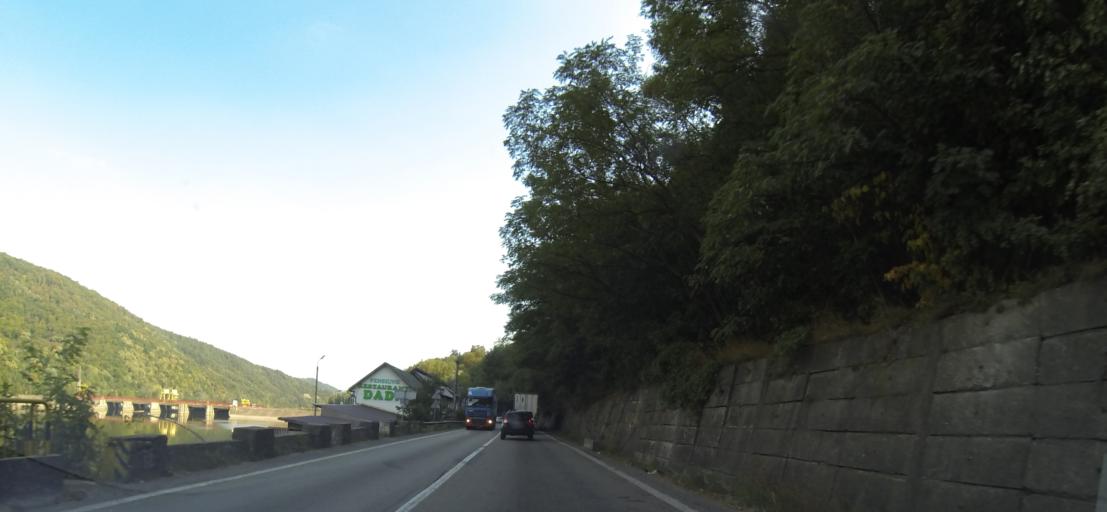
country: RO
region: Valcea
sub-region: Oras Calimanesti
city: Calimanesti
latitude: 45.2790
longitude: 24.3057
